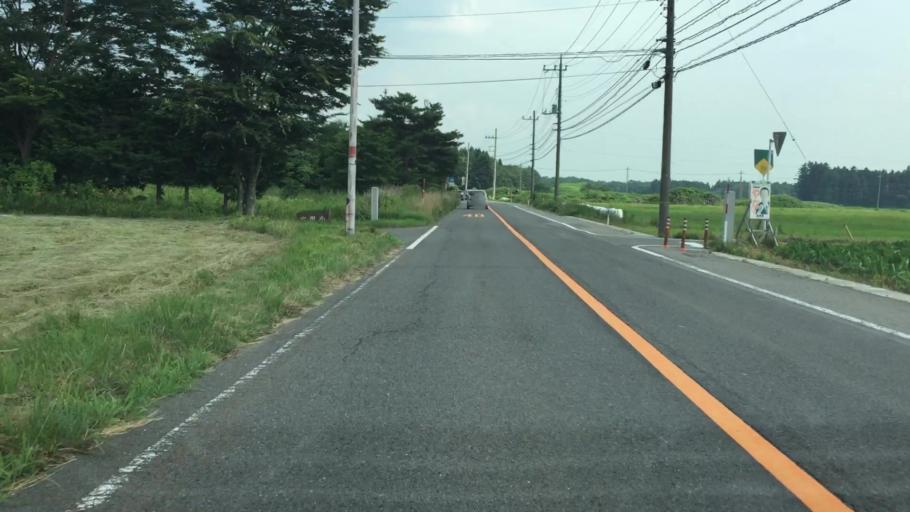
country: JP
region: Tochigi
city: Kuroiso
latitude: 37.0269
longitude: 139.9463
